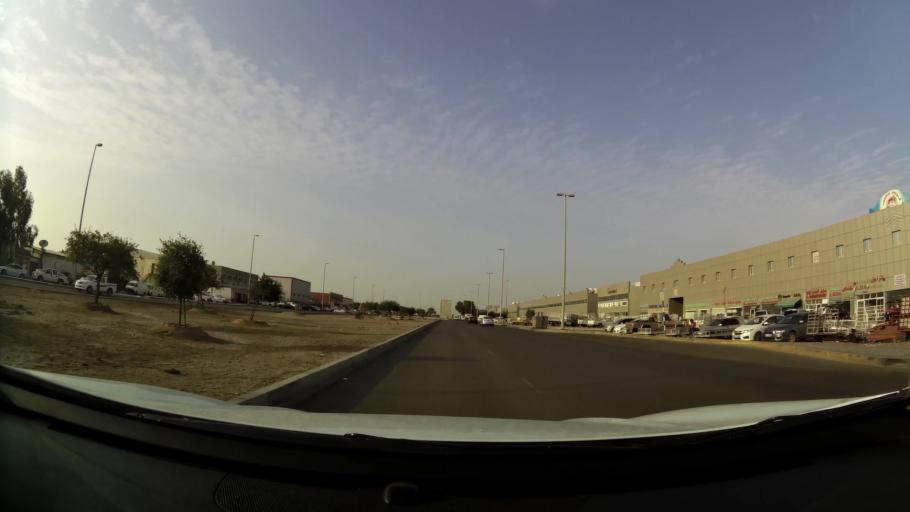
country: AE
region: Abu Dhabi
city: Abu Dhabi
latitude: 24.3706
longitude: 54.5162
